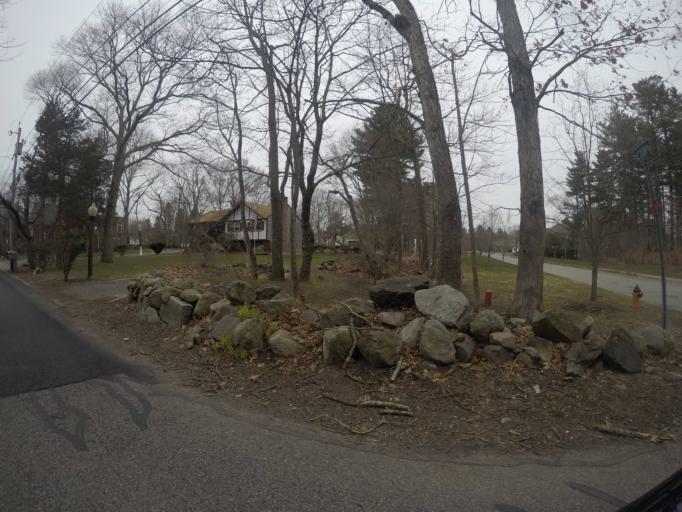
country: US
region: Massachusetts
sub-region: Bristol County
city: Easton
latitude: 42.0348
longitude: -71.1494
